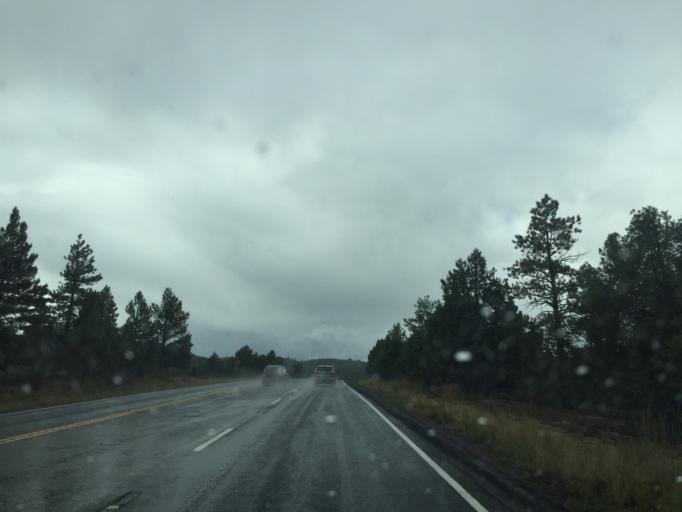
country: US
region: Utah
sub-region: Garfield County
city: Panguitch
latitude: 37.4769
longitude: -112.5134
